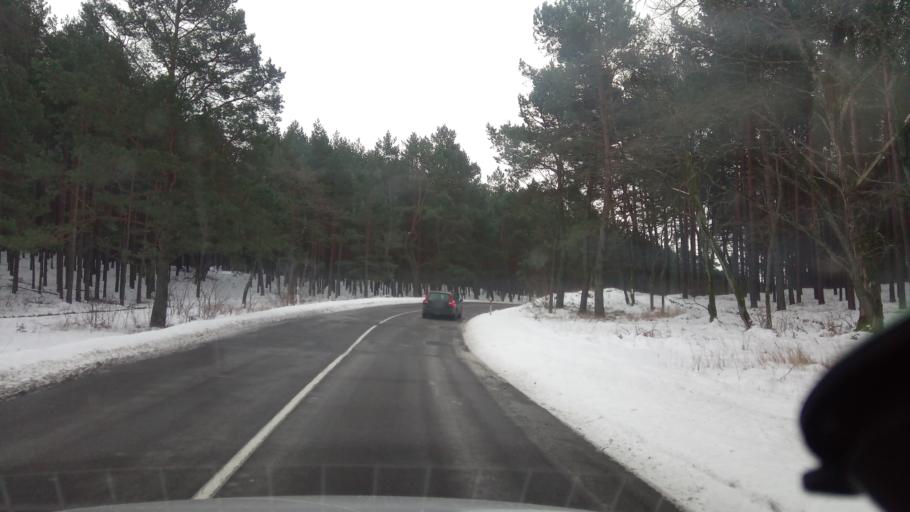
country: LT
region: Klaipedos apskritis
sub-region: Klaipeda
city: Klaipeda
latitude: 55.6642
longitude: 21.1158
